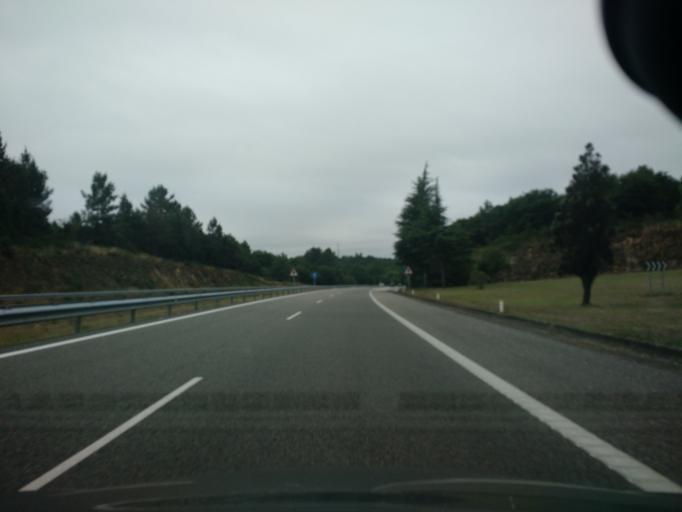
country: ES
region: Galicia
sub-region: Provincia da Coruna
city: Oroso
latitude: 42.9355
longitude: -8.4658
